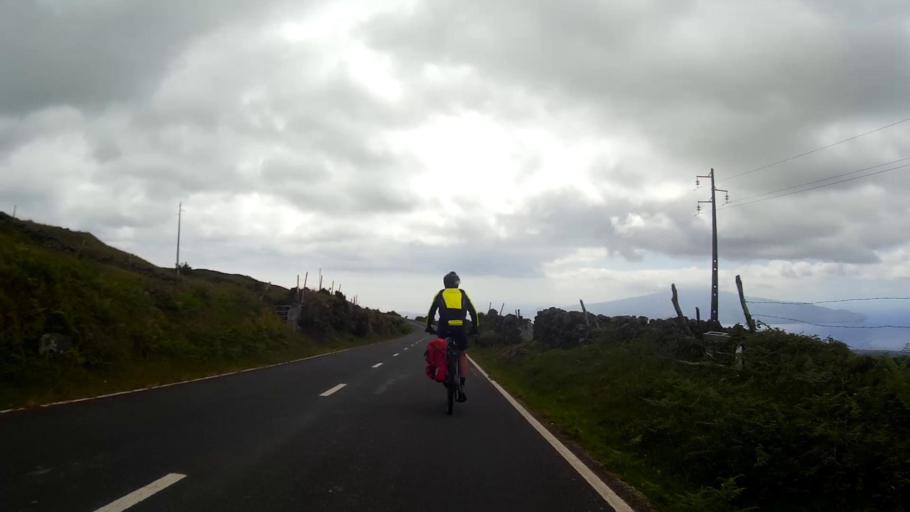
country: PT
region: Azores
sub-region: Madalena
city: Madalena
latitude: 38.4972
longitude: -28.4308
